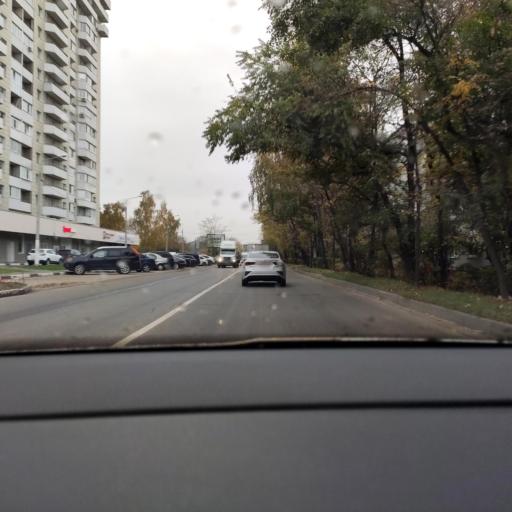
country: RU
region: Moskovskaya
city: Ivanteyevka
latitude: 55.9674
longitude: 37.8991
